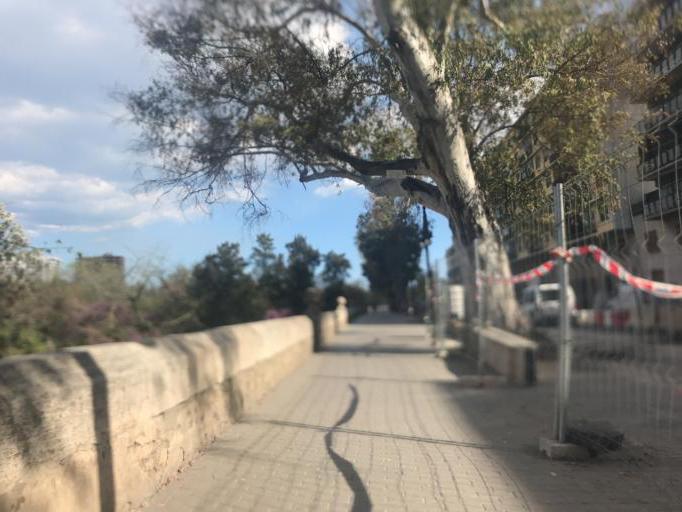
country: ES
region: Valencia
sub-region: Provincia de Valencia
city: Valencia
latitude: 39.4783
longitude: -0.3730
